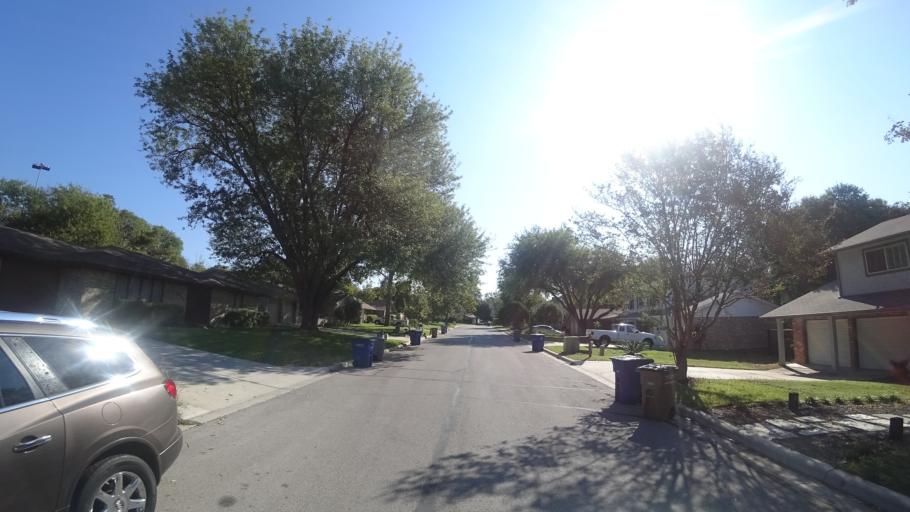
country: US
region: Texas
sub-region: Travis County
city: Austin
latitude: 30.3199
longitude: -97.6693
